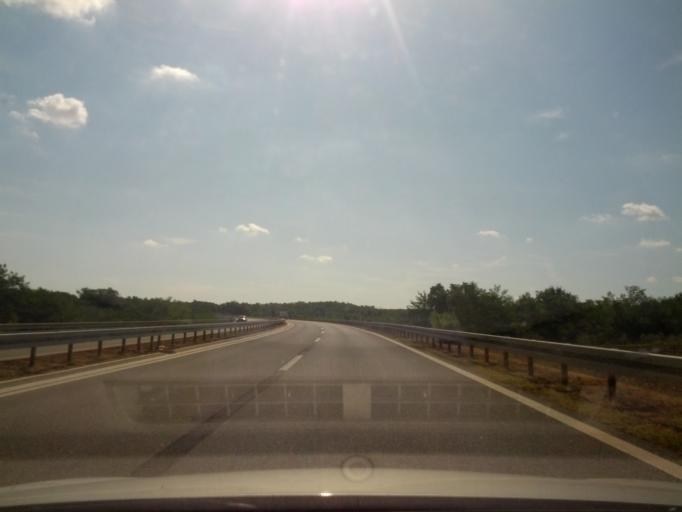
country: HR
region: Istarska
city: Buje
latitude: 45.3203
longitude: 13.6767
